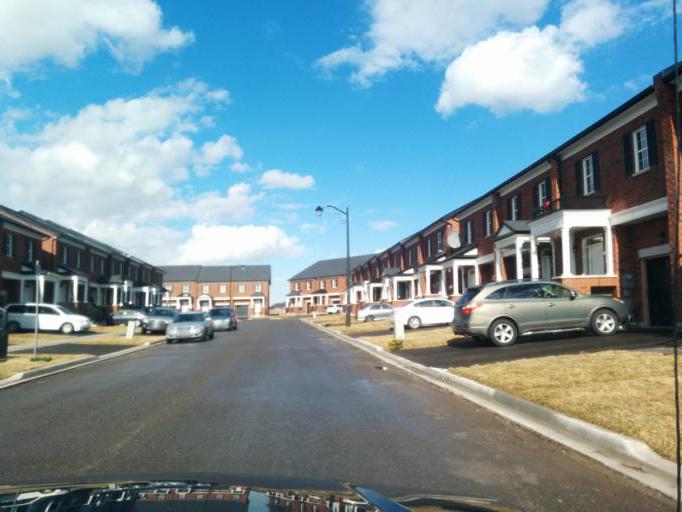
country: CA
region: Ontario
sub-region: Halton
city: Milton
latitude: 43.4935
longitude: -79.8673
